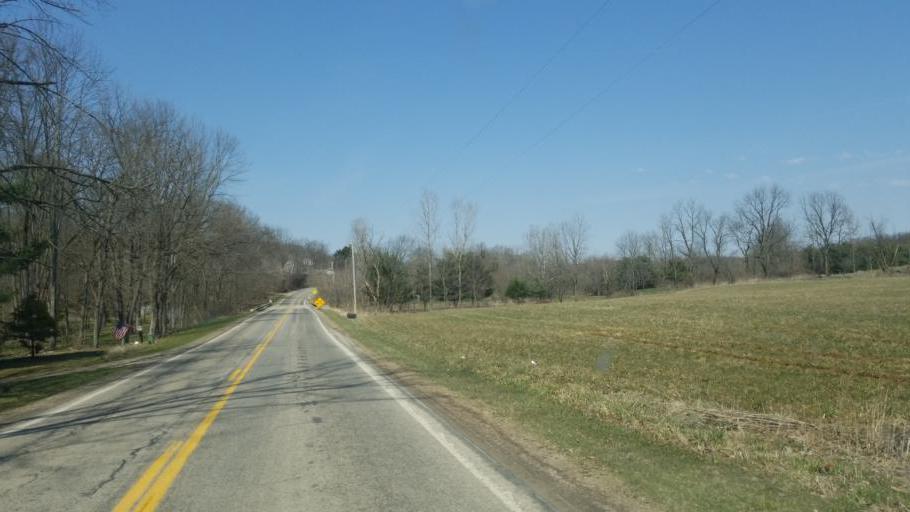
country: US
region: Ohio
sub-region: Ashland County
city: Loudonville
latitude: 40.7215
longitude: -82.1835
